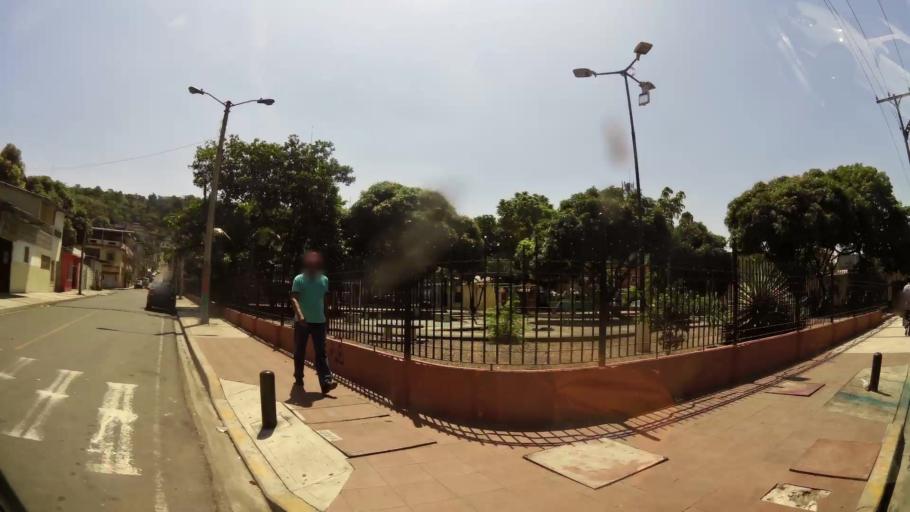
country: EC
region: Guayas
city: Guayaquil
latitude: -2.1881
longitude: -79.9282
